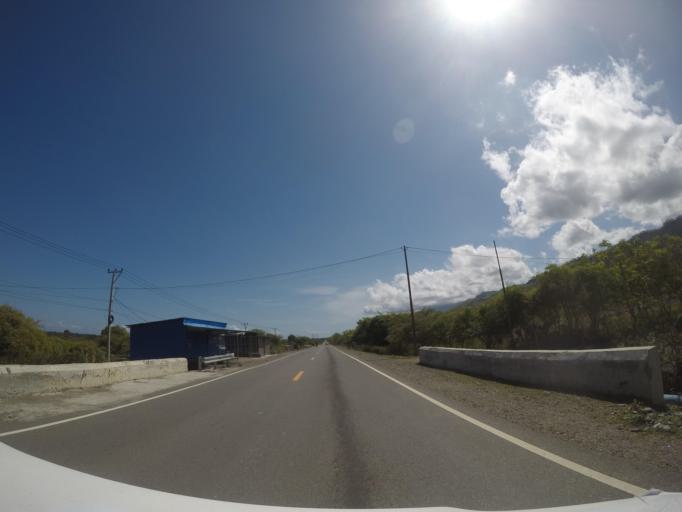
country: ID
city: Metinaro
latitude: -8.5231
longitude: 125.7669
